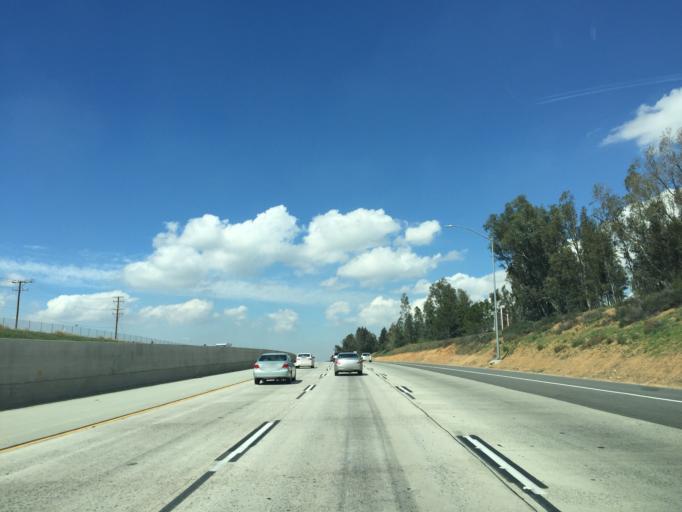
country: US
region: California
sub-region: Riverside County
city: Beaumont
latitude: 33.9479
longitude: -117.0058
